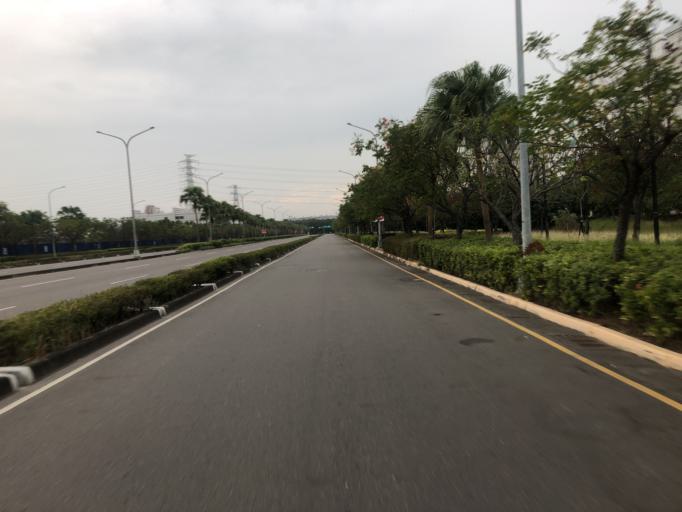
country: TW
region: Taiwan
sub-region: Tainan
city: Tainan
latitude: 23.1023
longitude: 120.2797
